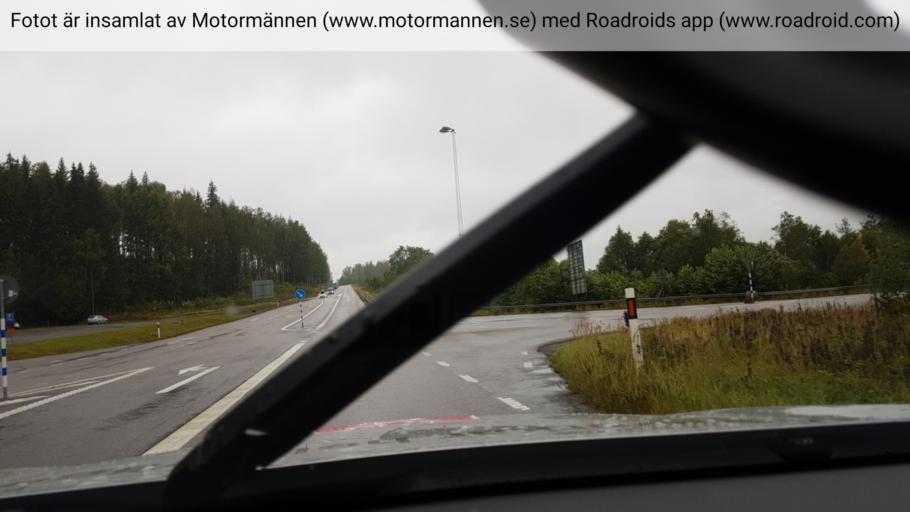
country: SE
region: Vaestra Goetaland
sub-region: Bengtsfors Kommun
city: Billingsfors
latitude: 59.0159
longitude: 12.2696
